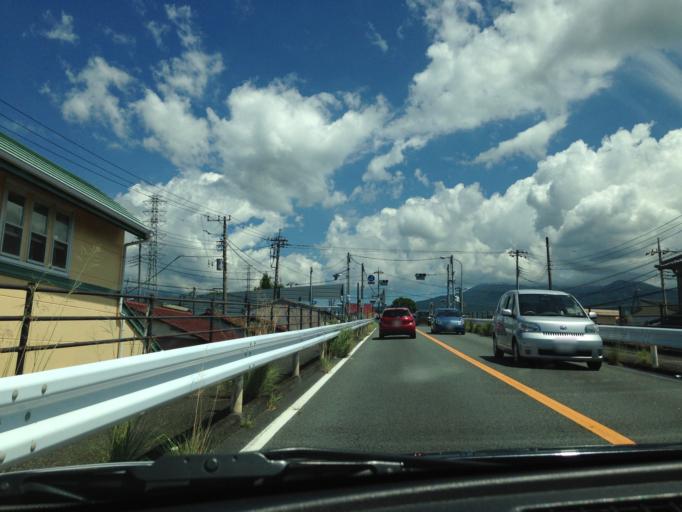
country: JP
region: Shizuoka
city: Fuji
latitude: 35.1762
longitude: 138.6938
